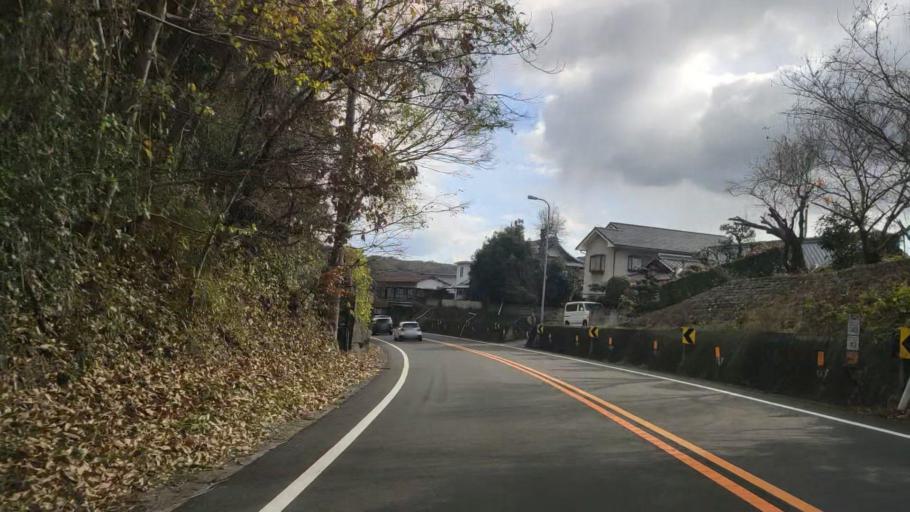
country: JP
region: Ehime
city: Hojo
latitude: 34.0603
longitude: 132.9165
